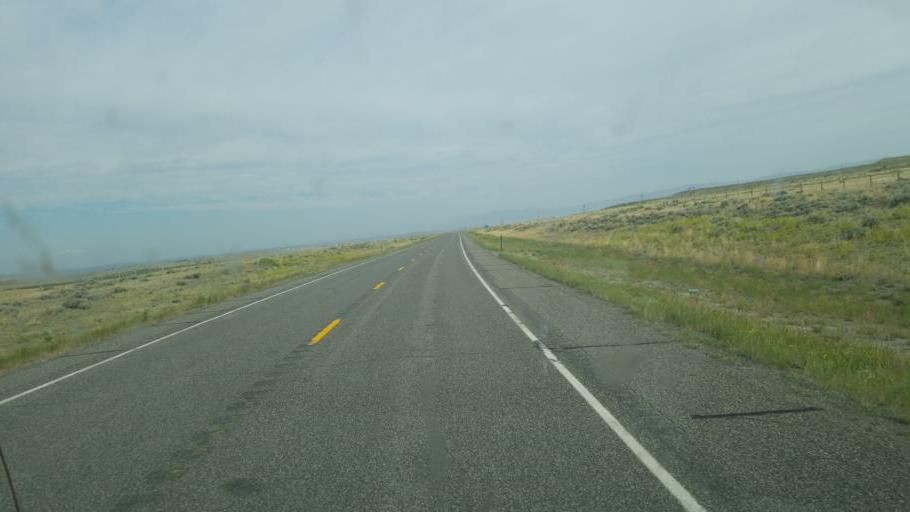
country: US
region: Wyoming
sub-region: Fremont County
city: Riverton
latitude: 43.2257
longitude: -108.0512
